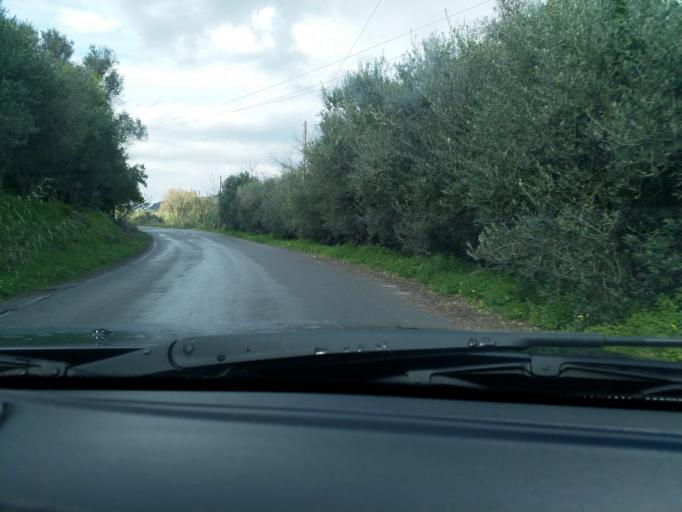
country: GR
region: Crete
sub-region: Nomos Chanias
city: Agia Marina
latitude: 35.4952
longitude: 23.9062
